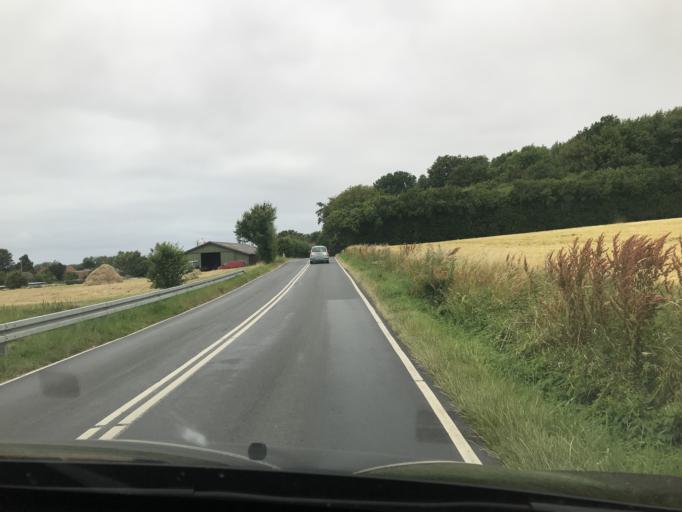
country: DK
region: South Denmark
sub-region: AEro Kommune
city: AEroskobing
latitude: 54.8669
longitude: 10.3669
